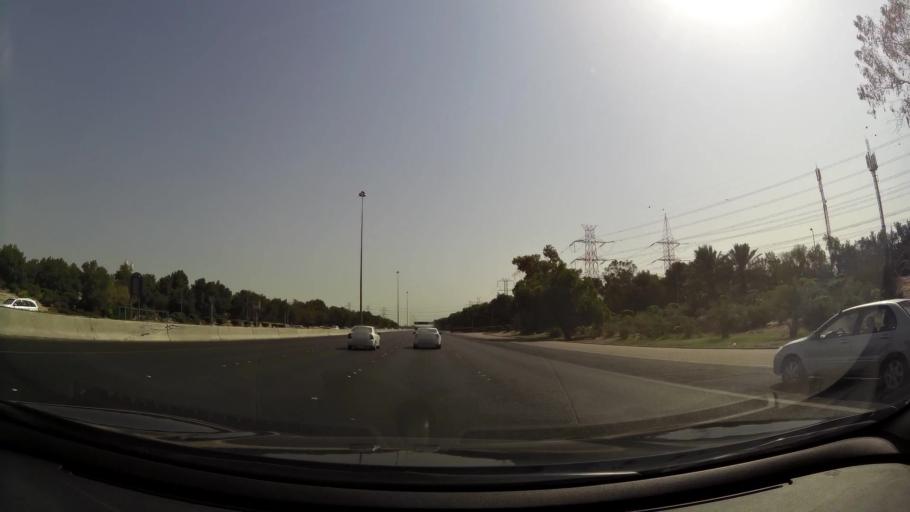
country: KW
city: Bayan
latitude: 29.2788
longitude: 48.0354
